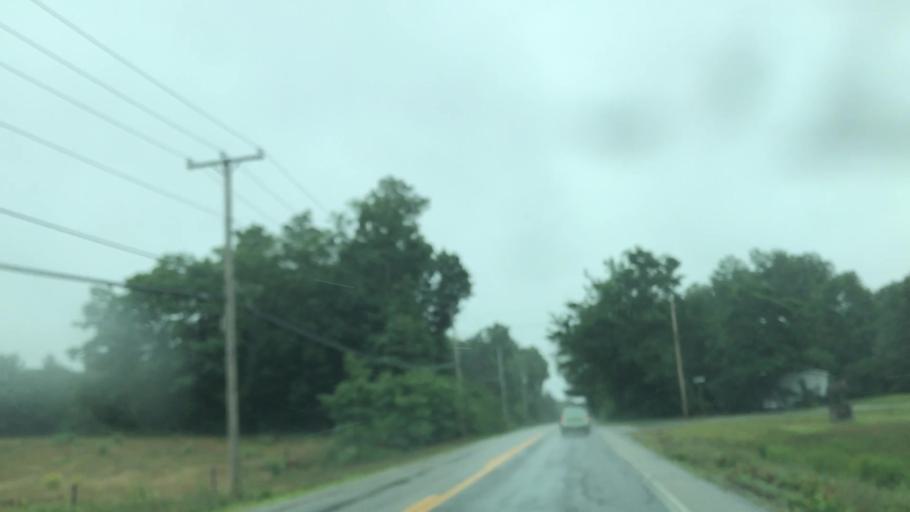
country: US
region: Maine
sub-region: York County
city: Berwick
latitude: 43.2829
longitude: -70.8368
